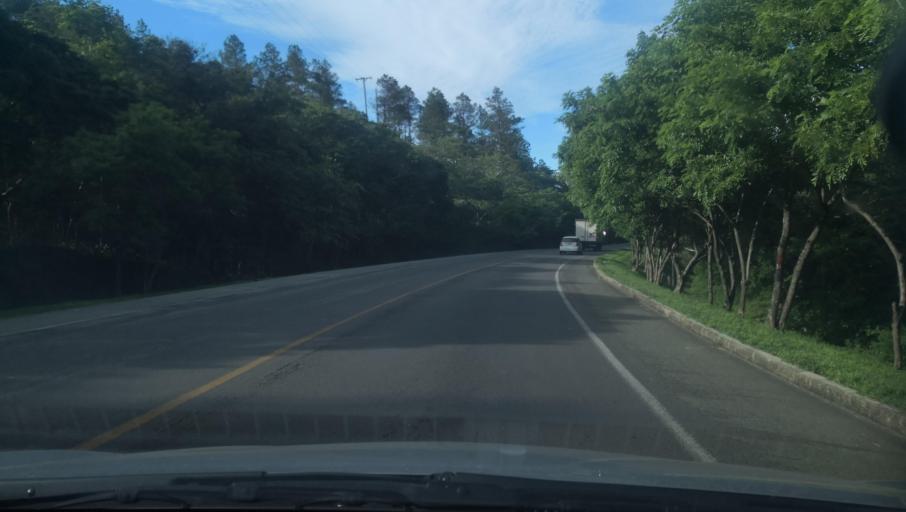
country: NI
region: Madriz
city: Totogalpa
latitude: 13.5727
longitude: -86.4830
